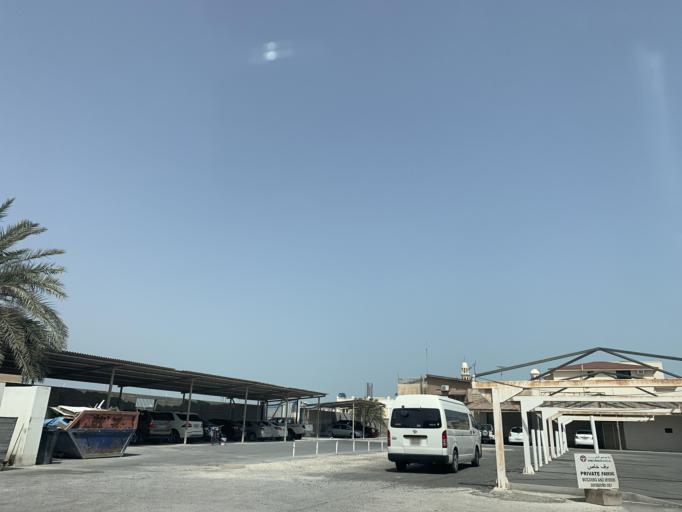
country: BH
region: Manama
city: Jidd Hafs
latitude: 26.2158
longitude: 50.5602
